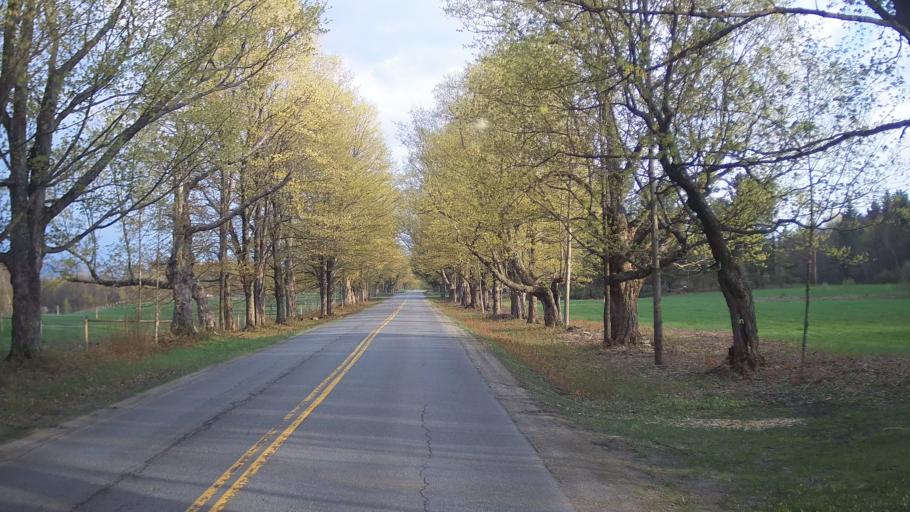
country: US
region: Vermont
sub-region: Orleans County
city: Newport
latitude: 44.9081
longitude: -72.4314
